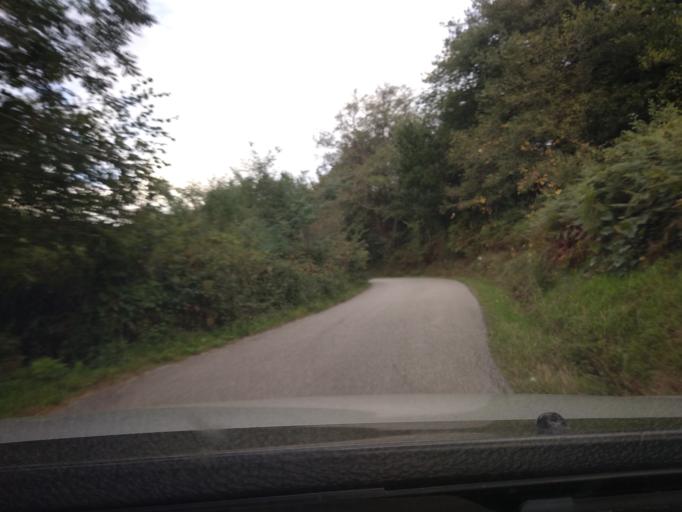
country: ES
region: Galicia
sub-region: Provincia de Pontevedra
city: Moana
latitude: 42.2962
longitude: -8.7348
